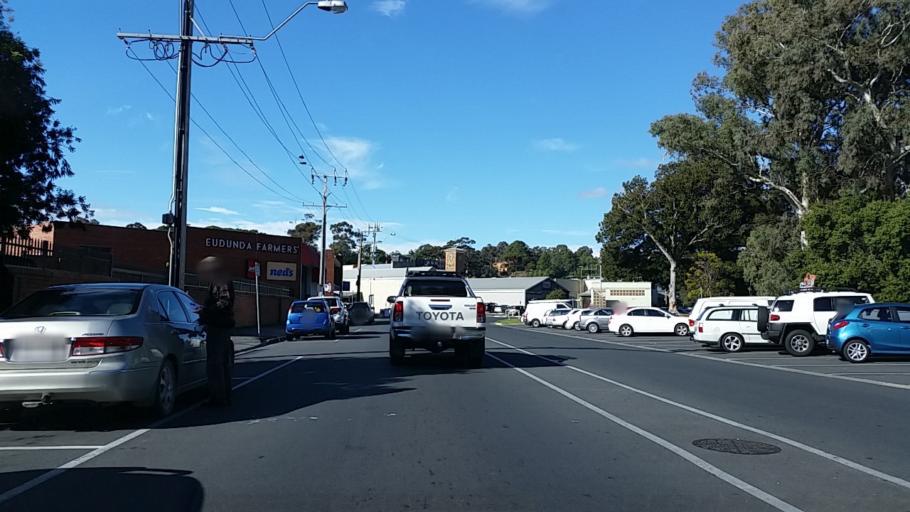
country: AU
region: South Australia
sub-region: Gawler
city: Gawler
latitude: -34.5995
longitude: 138.7478
